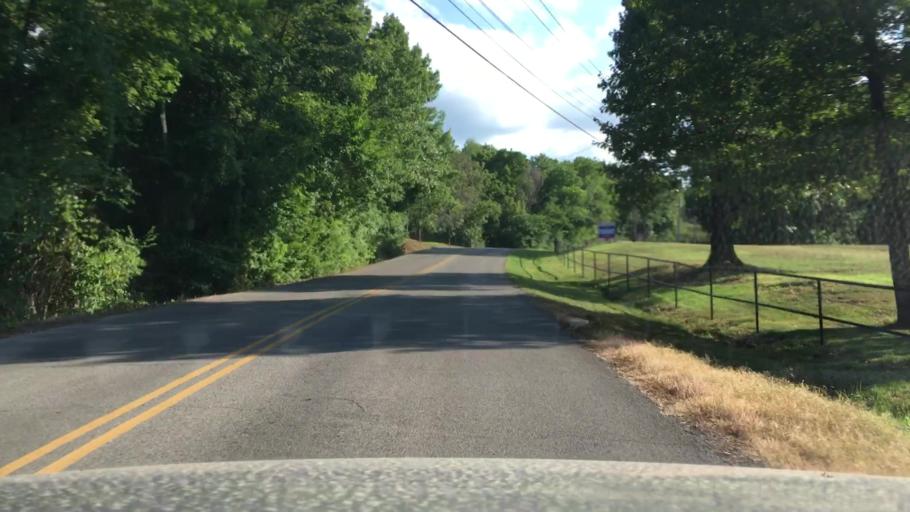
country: US
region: Oklahoma
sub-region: Muskogee County
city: Fort Gibson
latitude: 35.9174
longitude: -95.1546
